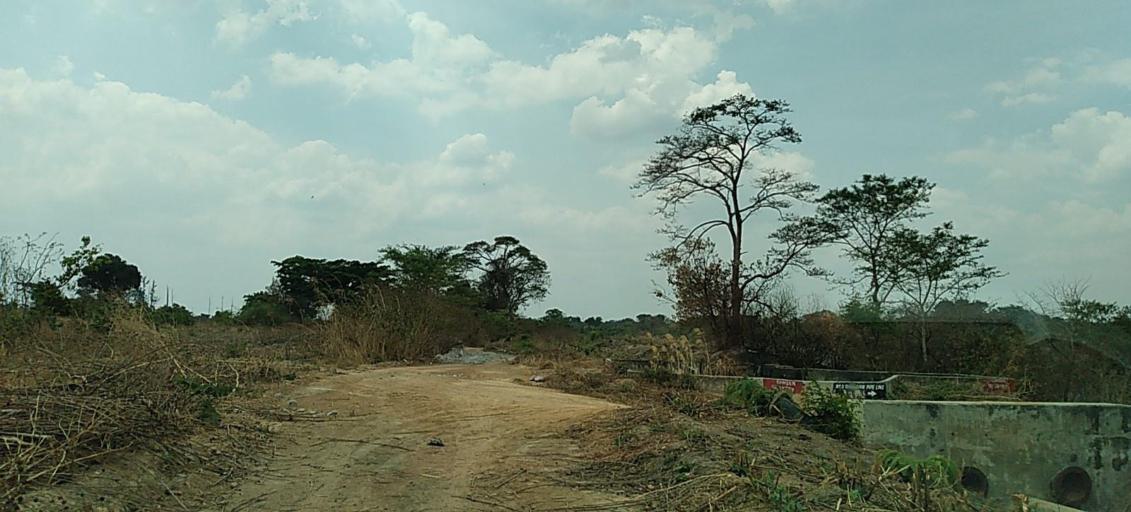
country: ZM
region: Copperbelt
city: Chililabombwe
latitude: -12.3550
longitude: 27.8035
